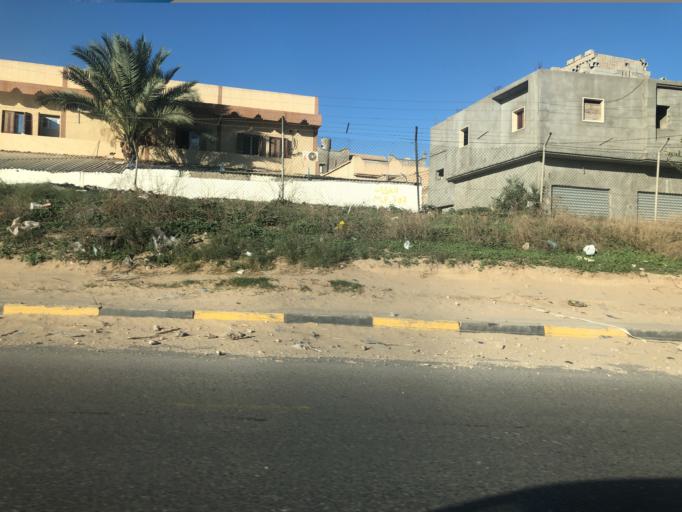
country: LY
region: Tripoli
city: Tagiura
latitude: 32.8698
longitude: 13.2711
